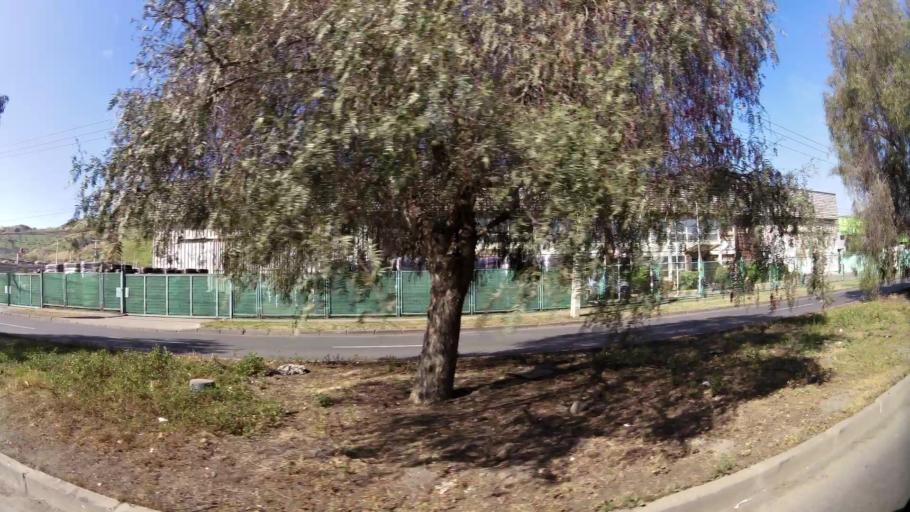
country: CL
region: Santiago Metropolitan
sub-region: Provincia de Chacabuco
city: Chicureo Abajo
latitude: -33.3282
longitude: -70.7075
